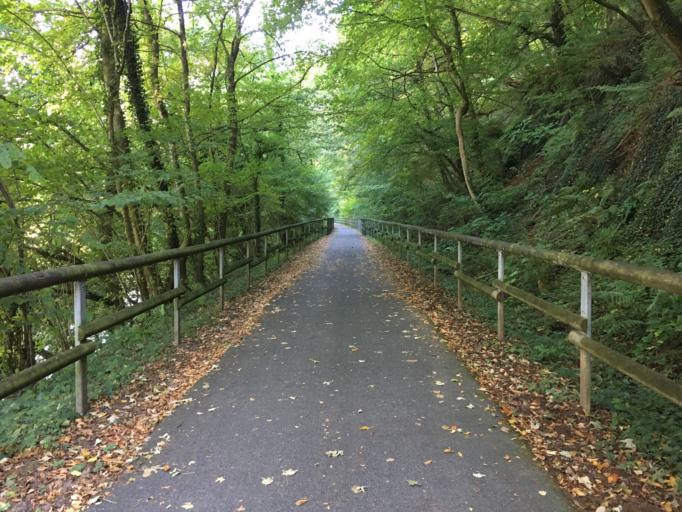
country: LU
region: Grevenmacher
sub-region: Canton d'Echternach
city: Rosport
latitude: 49.7584
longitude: 6.5149
